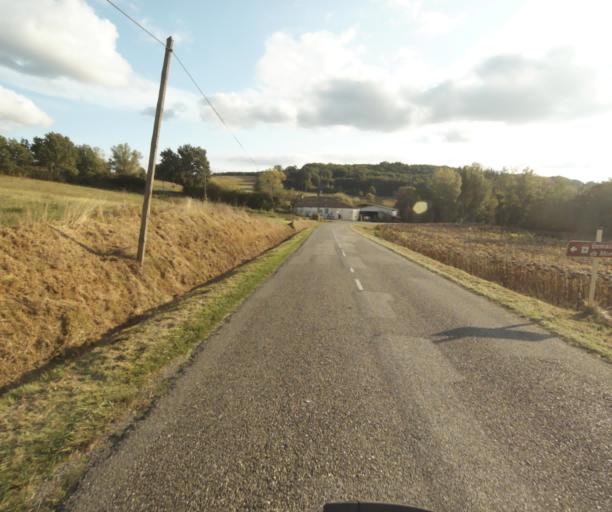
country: FR
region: Midi-Pyrenees
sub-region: Departement de la Haute-Garonne
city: Launac
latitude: 43.8203
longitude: 1.1341
